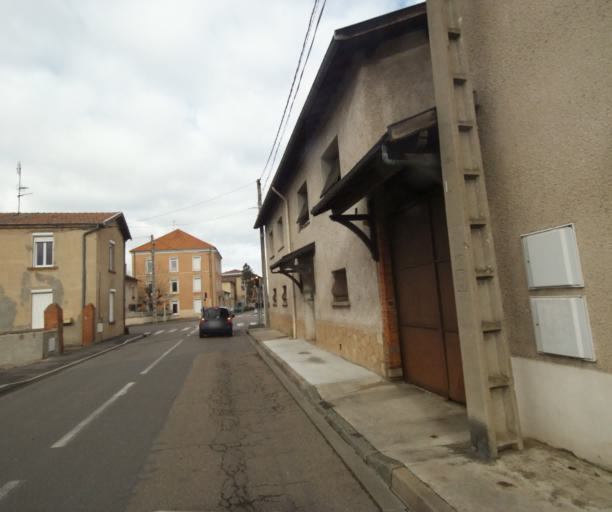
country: FR
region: Rhone-Alpes
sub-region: Departement de la Loire
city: Riorges
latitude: 46.0424
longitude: 4.0529
